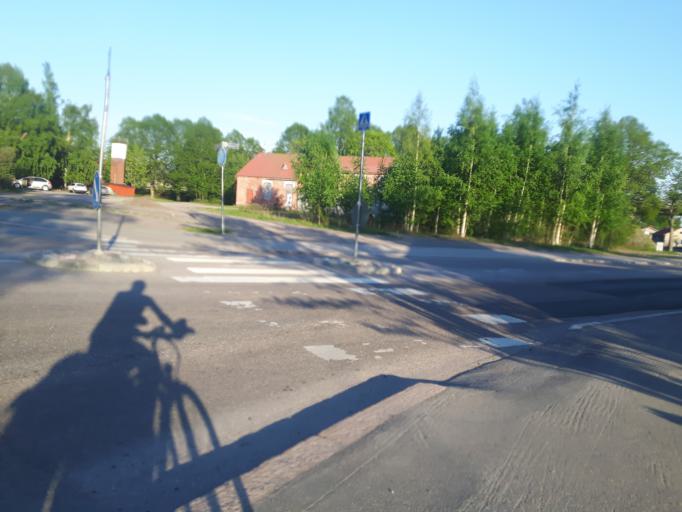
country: FI
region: Uusimaa
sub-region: Loviisa
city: Lovisa
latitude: 60.4565
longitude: 26.2188
